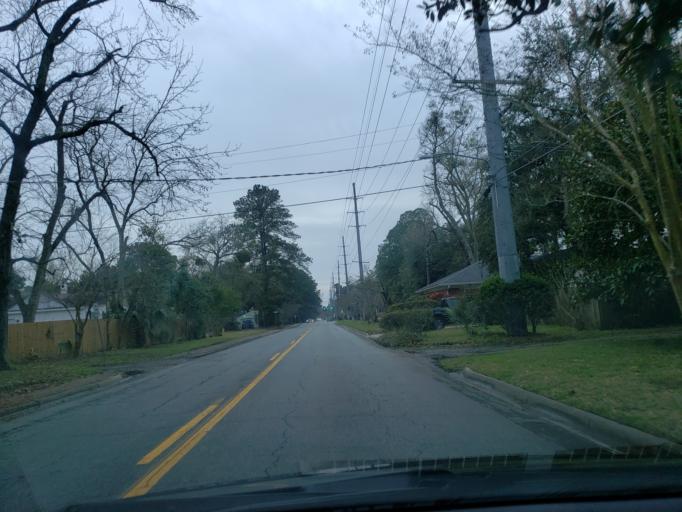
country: US
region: Georgia
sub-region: Chatham County
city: Savannah
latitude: 32.0355
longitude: -81.0988
